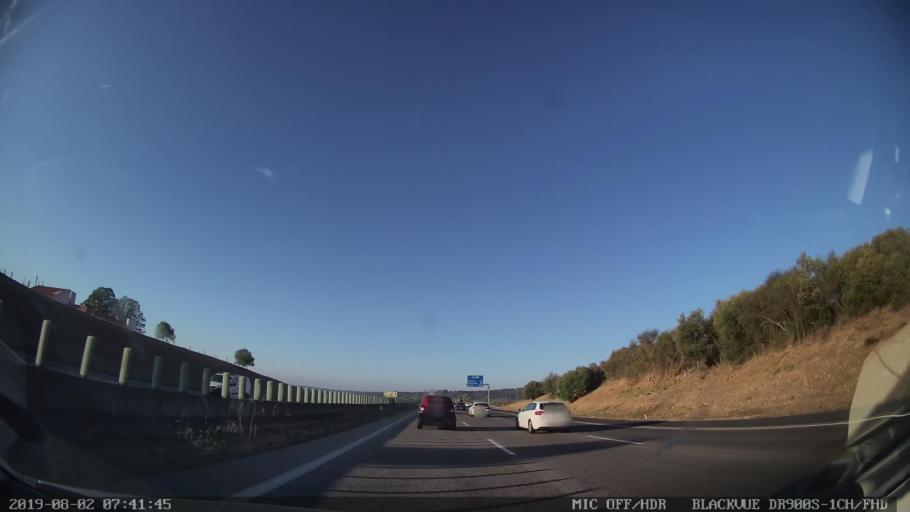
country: PT
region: Lisbon
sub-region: Alenquer
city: Carregado
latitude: 39.0399
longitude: -8.9569
